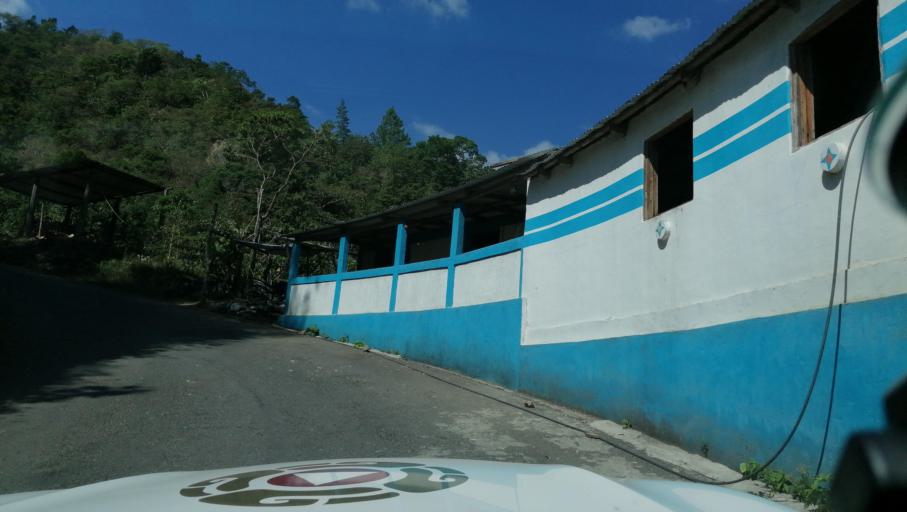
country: MX
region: Chiapas
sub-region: Cacahoatan
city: Benito Juarez
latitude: 15.1819
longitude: -92.1877
